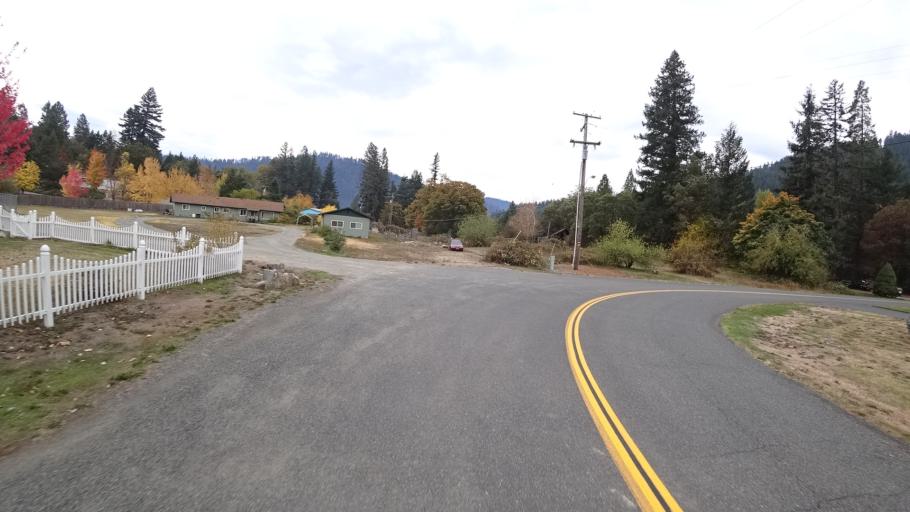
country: US
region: California
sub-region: Siskiyou County
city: Happy Camp
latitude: 41.8050
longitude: -123.3803
